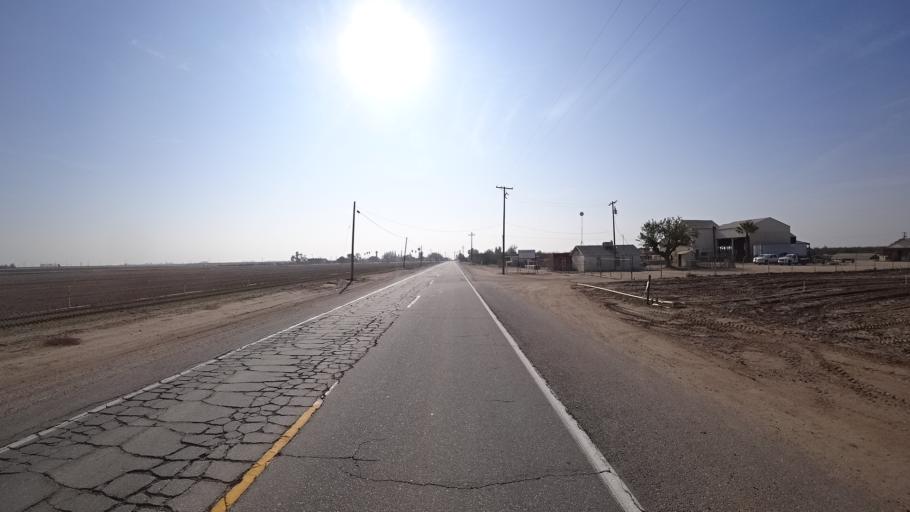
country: US
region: California
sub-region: Kern County
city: Greenfield
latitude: 35.2718
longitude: -119.1098
